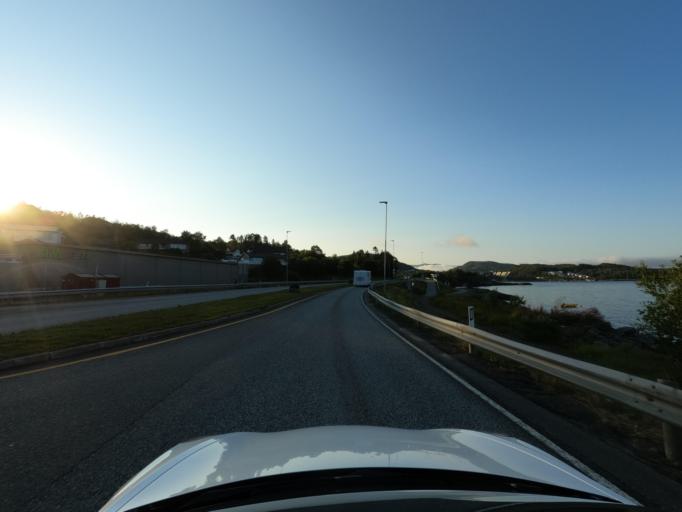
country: NO
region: Troms
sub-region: Harstad
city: Harstad
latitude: 68.7626
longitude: 16.5608
